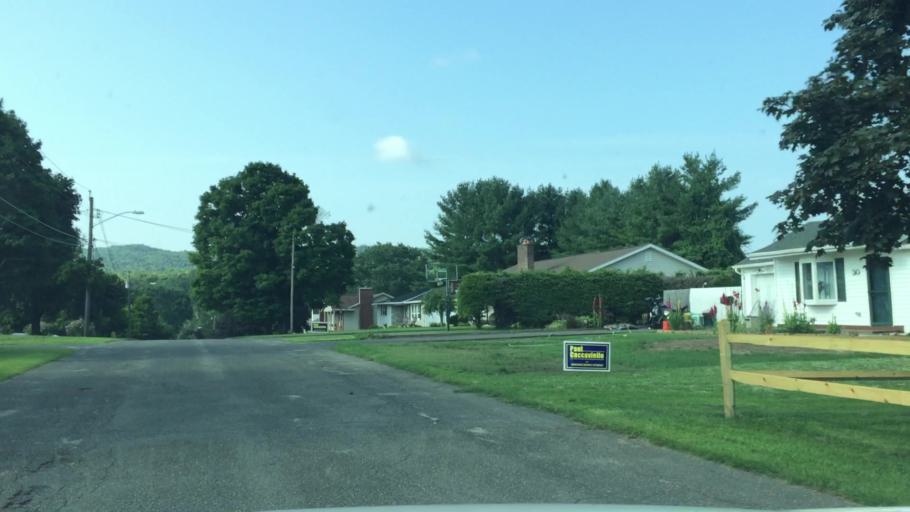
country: US
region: Massachusetts
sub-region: Berkshire County
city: Pittsfield
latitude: 42.4282
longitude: -73.2093
